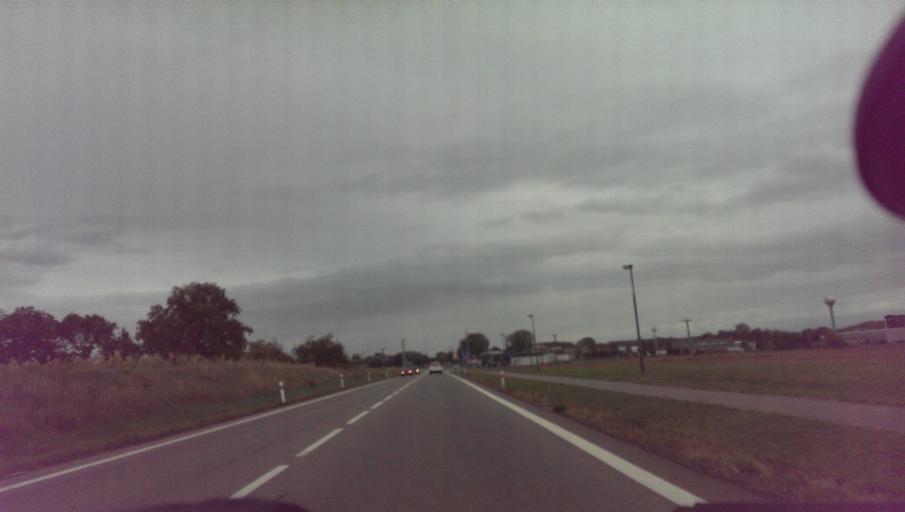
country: CZ
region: South Moravian
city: Domanin
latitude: 48.9745
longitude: 17.2969
